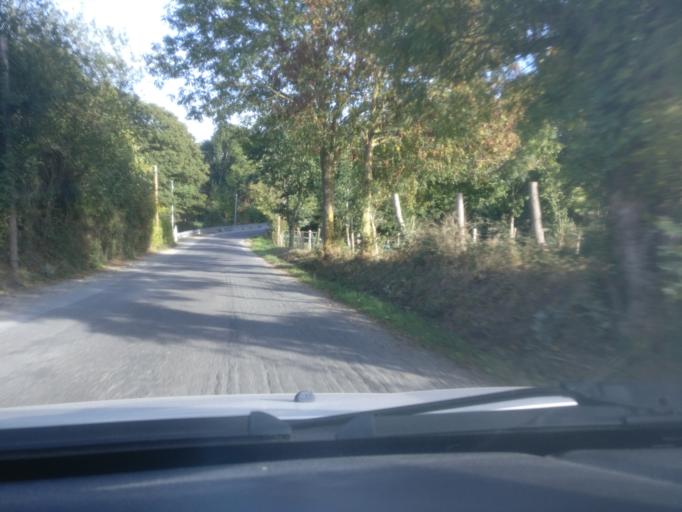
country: FR
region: Lower Normandy
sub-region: Departement de la Manche
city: Sartilly
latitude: 48.7096
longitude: -1.4837
